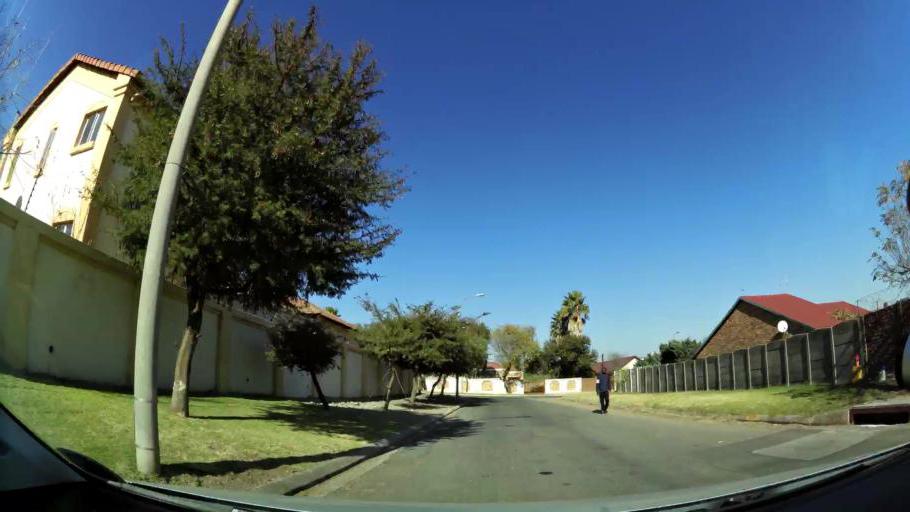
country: ZA
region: Gauteng
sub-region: City of Johannesburg Metropolitan Municipality
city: Modderfontein
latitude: -26.0642
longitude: 28.1983
